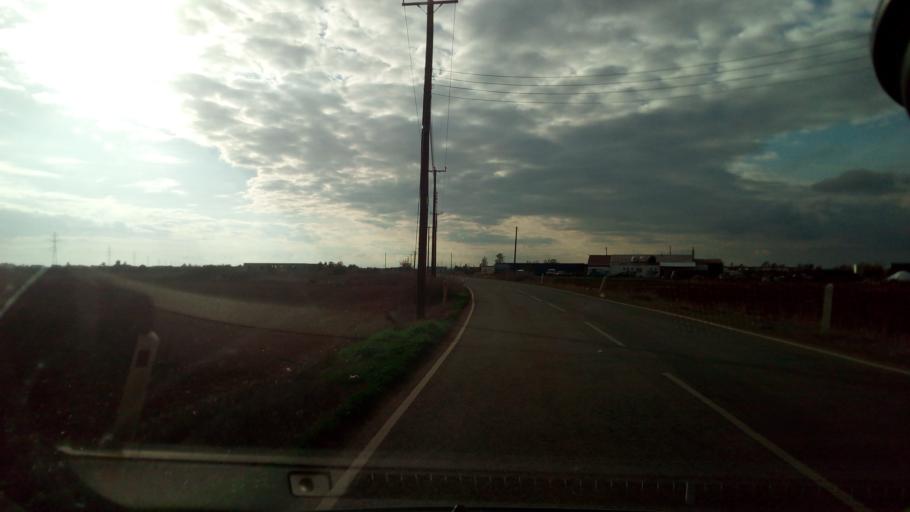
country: CY
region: Ammochostos
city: Avgorou
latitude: 35.0424
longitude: 33.8676
